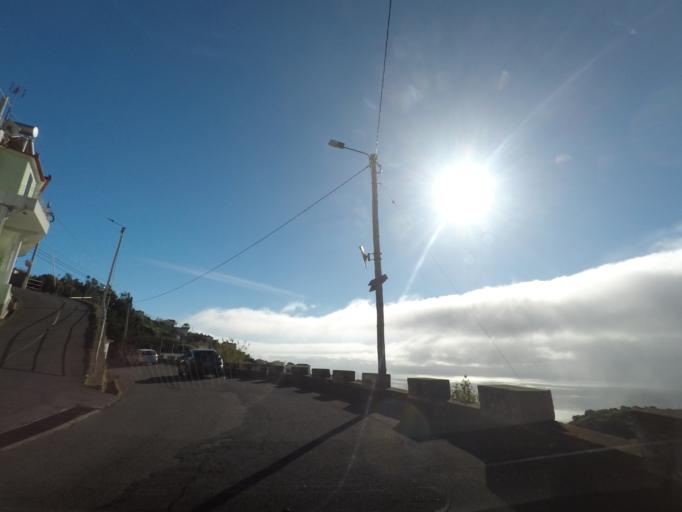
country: PT
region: Madeira
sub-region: Calheta
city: Arco da Calheta
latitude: 32.7291
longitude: -17.1534
